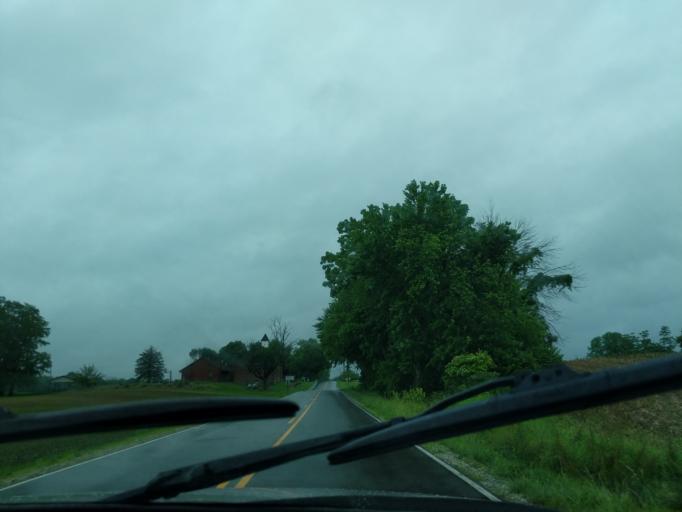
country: US
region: Indiana
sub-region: Hamilton County
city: Noblesville
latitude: 40.0663
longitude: -85.9327
